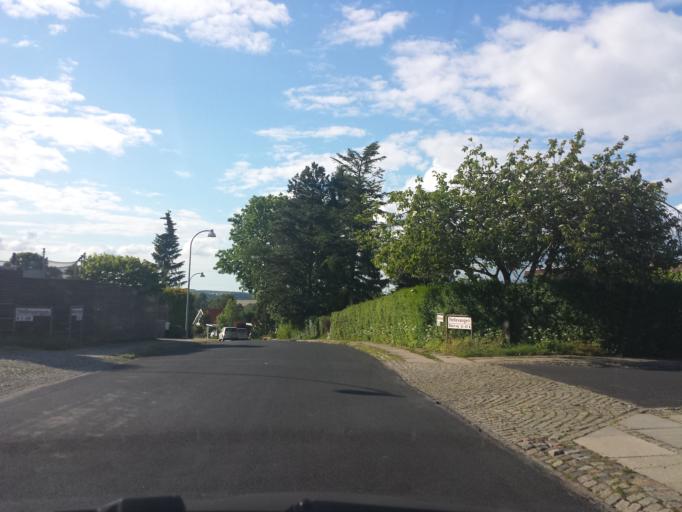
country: DK
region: Capital Region
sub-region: Ballerup Kommune
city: Malov
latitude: 55.7548
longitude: 12.3241
